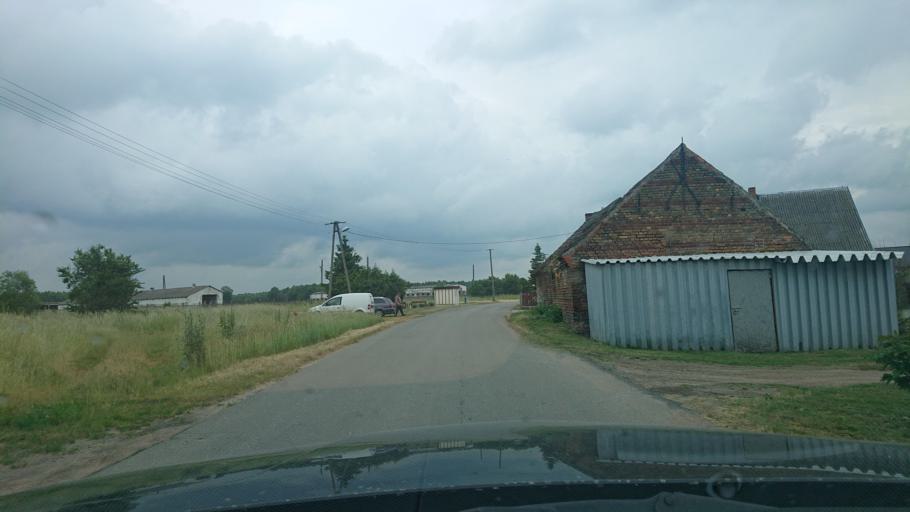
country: PL
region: Greater Poland Voivodeship
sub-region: Powiat gnieznienski
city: Gniezno
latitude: 52.4799
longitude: 17.5470
